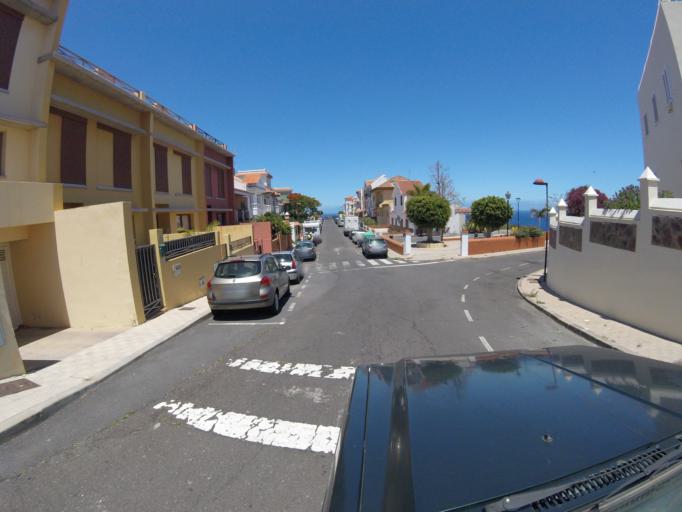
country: ES
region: Canary Islands
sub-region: Provincia de Santa Cruz de Tenerife
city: Candelaria
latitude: 28.3580
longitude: -16.3746
